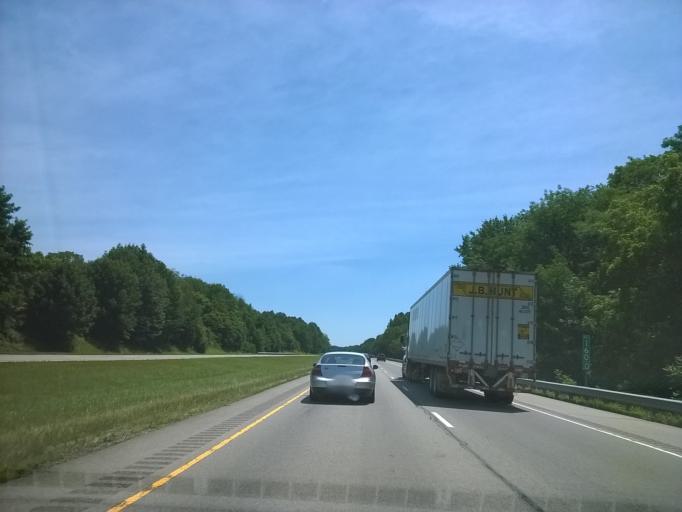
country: US
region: Indiana
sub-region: Ripley County
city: Sunman
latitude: 39.2853
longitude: -85.0215
